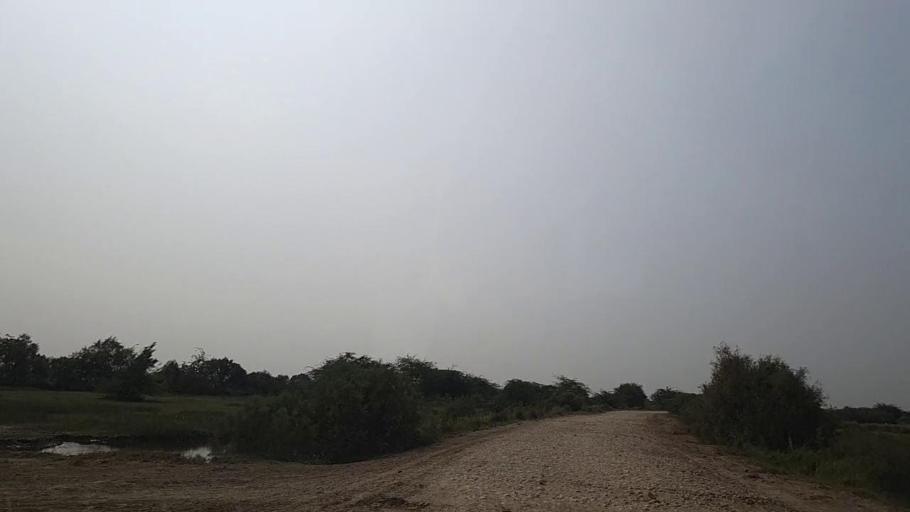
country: PK
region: Sindh
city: Mirpur Sakro
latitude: 24.6005
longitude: 67.7192
